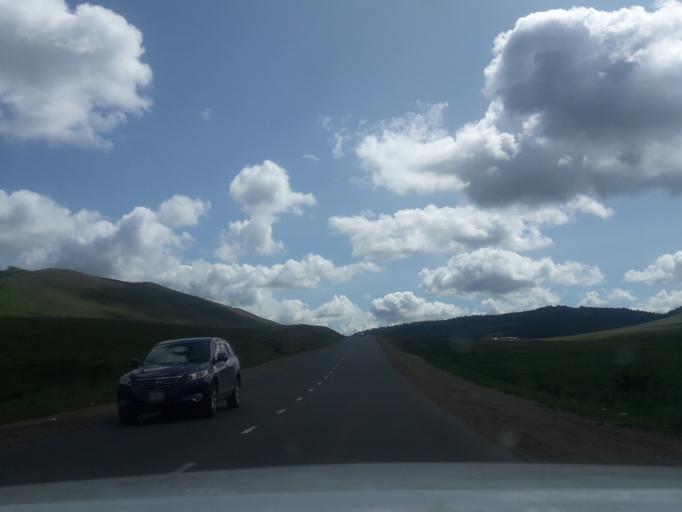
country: MN
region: Central Aimak
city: Ihsueuej
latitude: 48.1620
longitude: 106.4044
